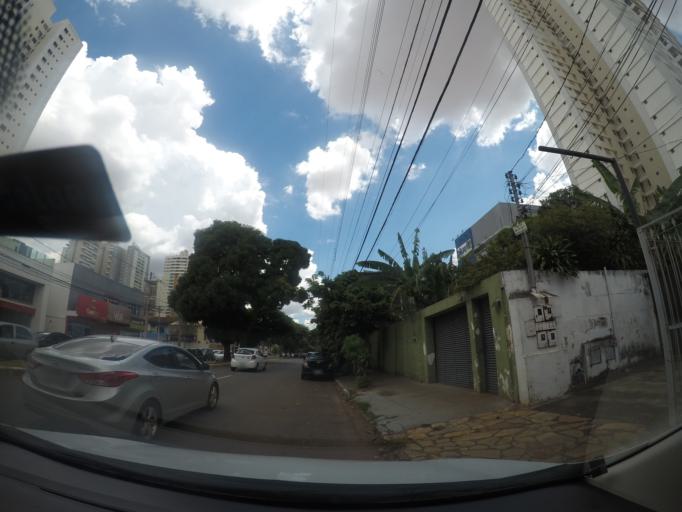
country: BR
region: Goias
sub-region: Goiania
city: Goiania
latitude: -16.6962
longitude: -49.2758
